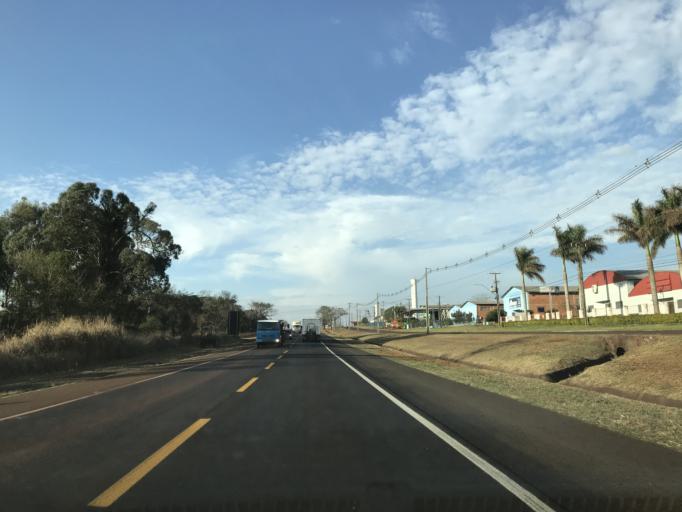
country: BR
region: Parana
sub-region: Cascavel
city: Cascavel
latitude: -25.0407
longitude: -53.6009
